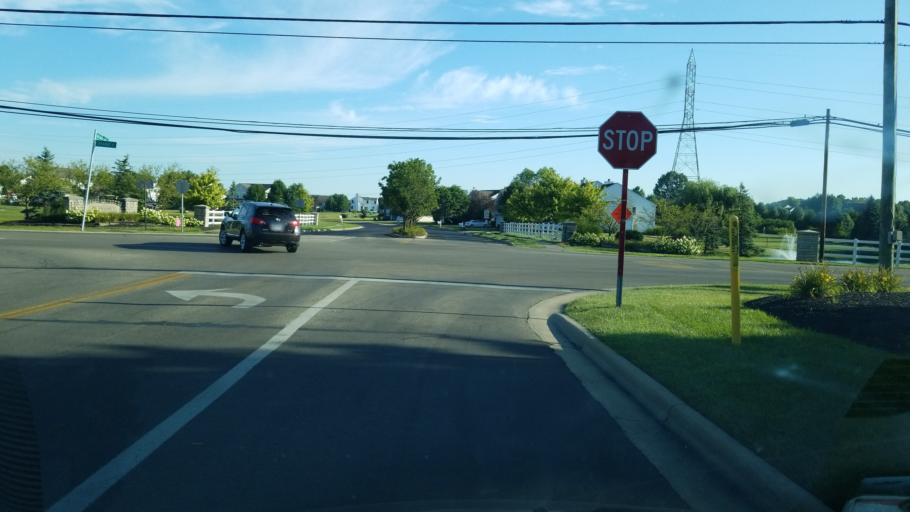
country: US
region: Ohio
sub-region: Delaware County
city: Lewis Center
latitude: 40.1741
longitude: -83.0007
